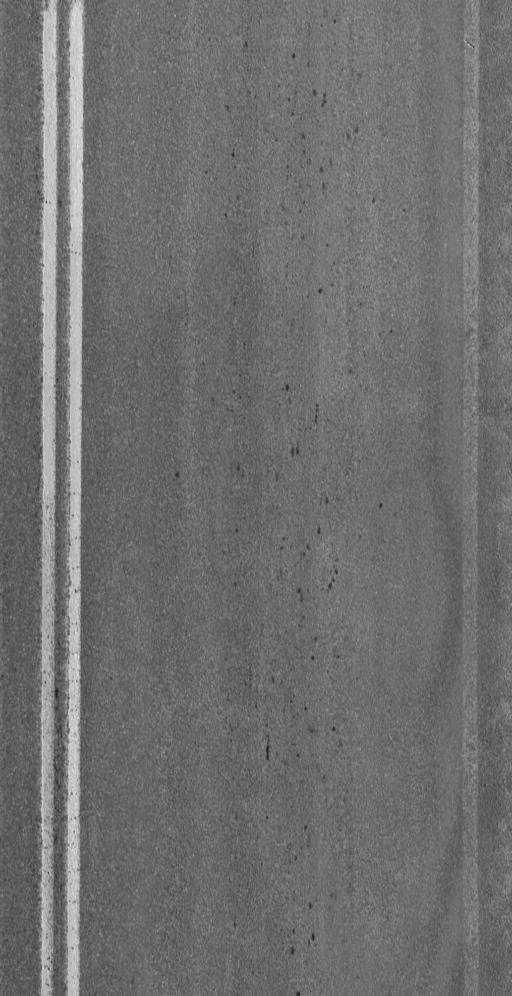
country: US
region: Vermont
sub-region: Washington County
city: Barre
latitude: 44.2736
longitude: -72.4913
